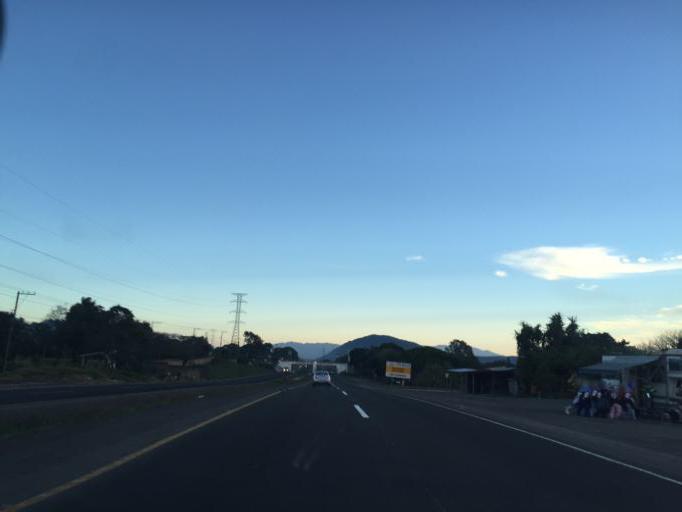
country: MX
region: Veracruz
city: Ixtac Zoquitlan
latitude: 18.8429
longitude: -97.0766
